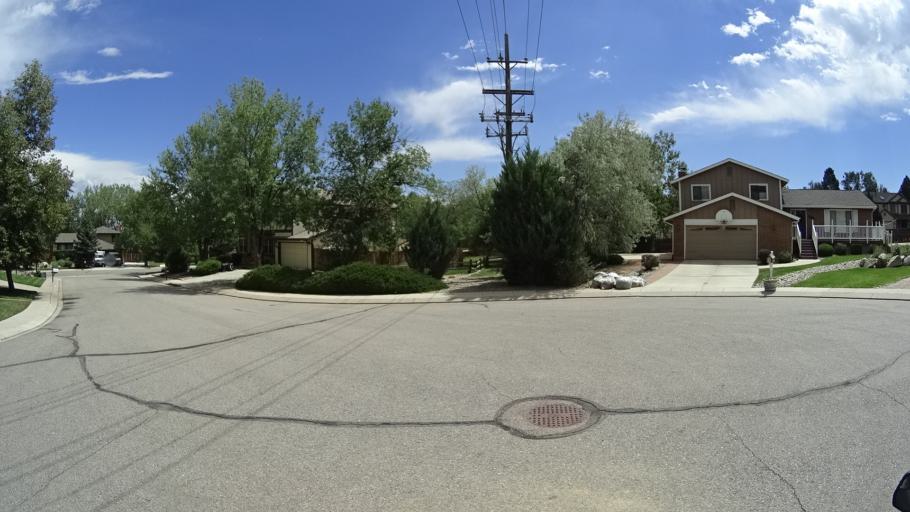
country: US
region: Colorado
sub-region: El Paso County
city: Stratmoor
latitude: 38.7703
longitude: -104.8178
